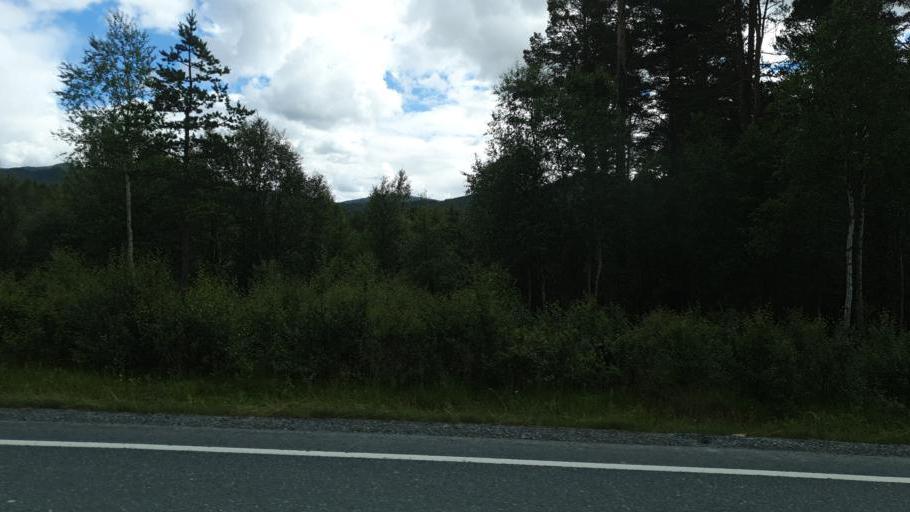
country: NO
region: Sor-Trondelag
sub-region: Oppdal
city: Oppdal
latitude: 62.6510
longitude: 9.8599
